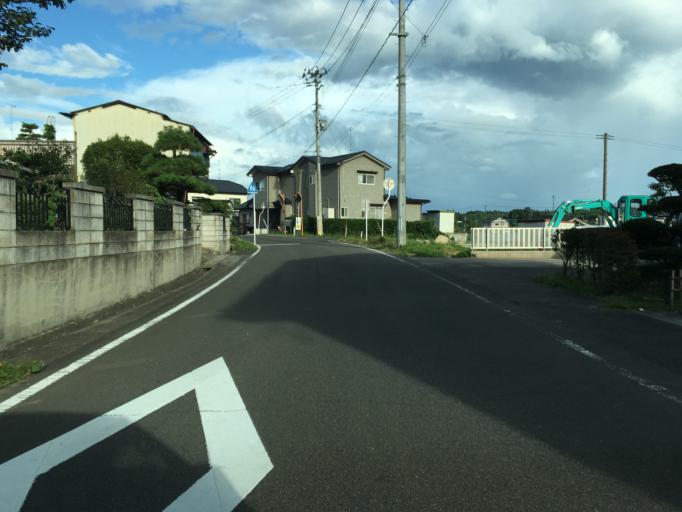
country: JP
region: Fukushima
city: Nihommatsu
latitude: 37.6337
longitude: 140.4608
